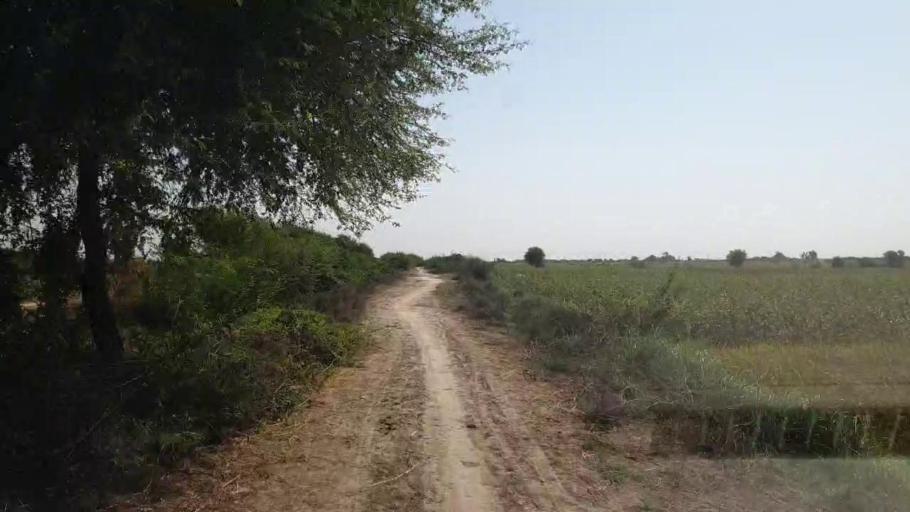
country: PK
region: Sindh
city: Kadhan
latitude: 24.5968
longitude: 69.0055
